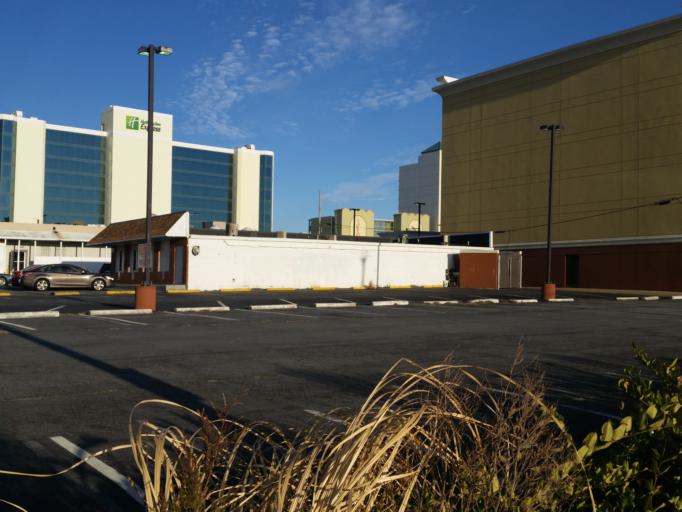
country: US
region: Virginia
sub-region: City of Virginia Beach
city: Virginia Beach
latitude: 36.8552
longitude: -75.9781
